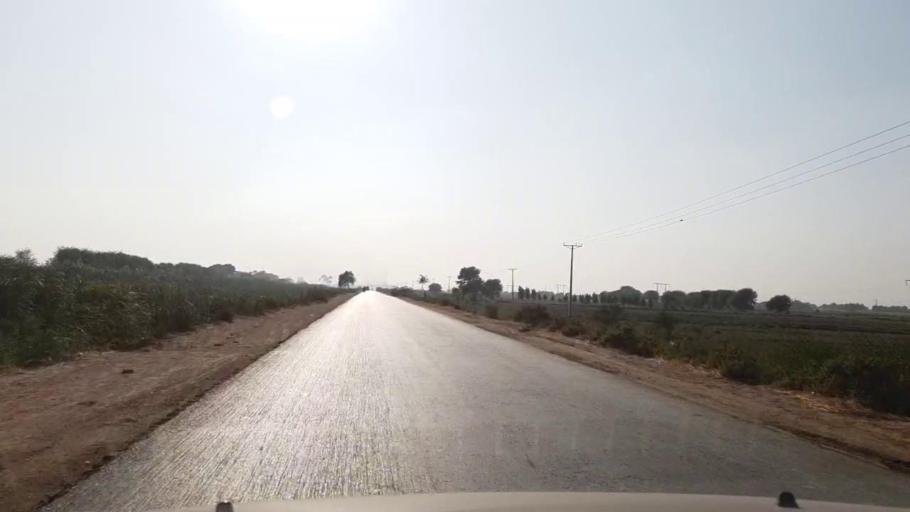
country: PK
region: Sindh
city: Tando Muhammad Khan
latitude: 25.0454
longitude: 68.4433
